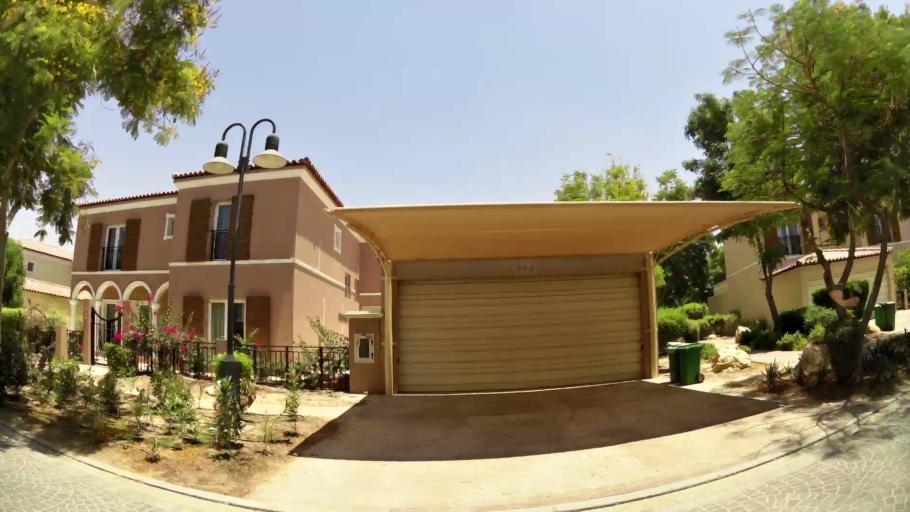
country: AE
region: Dubai
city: Dubai
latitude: 25.0074
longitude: 55.1614
